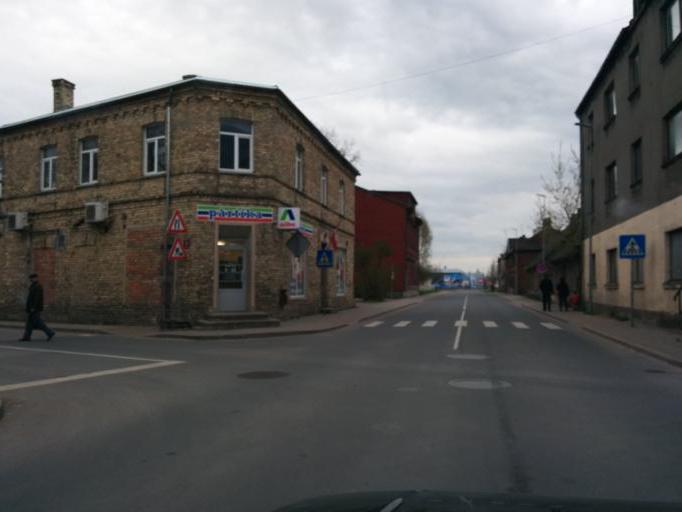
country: LV
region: Jelgava
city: Jelgava
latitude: 56.6418
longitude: 23.7243
